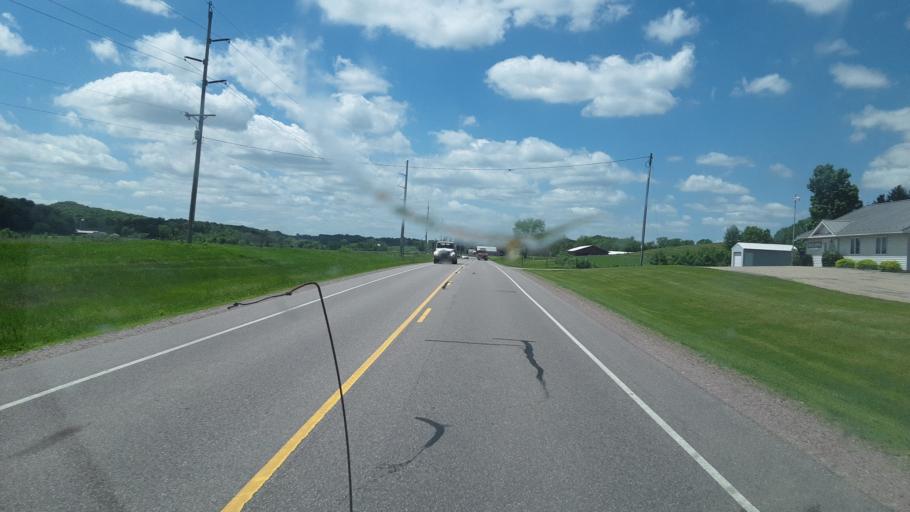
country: US
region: Wisconsin
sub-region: Sauk County
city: Reedsburg
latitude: 43.5925
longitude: -89.9176
